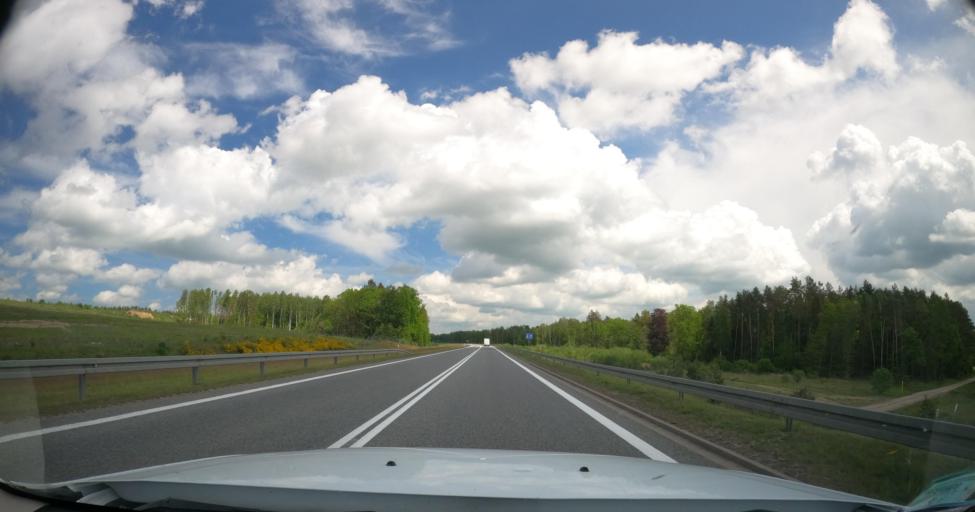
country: PL
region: Pomeranian Voivodeship
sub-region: Slupsk
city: Slupsk
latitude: 54.4383
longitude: 17.0706
